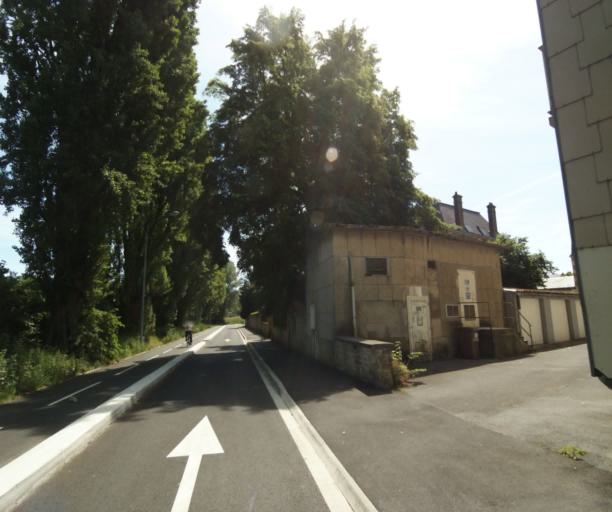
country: FR
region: Champagne-Ardenne
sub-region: Departement des Ardennes
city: Charleville-Mezieres
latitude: 49.7576
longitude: 4.7204
